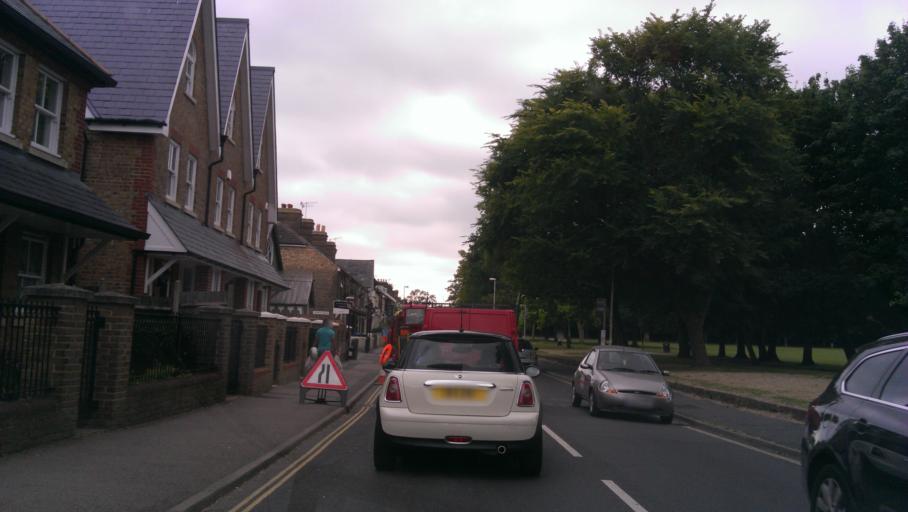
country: GB
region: England
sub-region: Kent
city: Faversham
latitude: 51.3144
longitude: 0.8965
